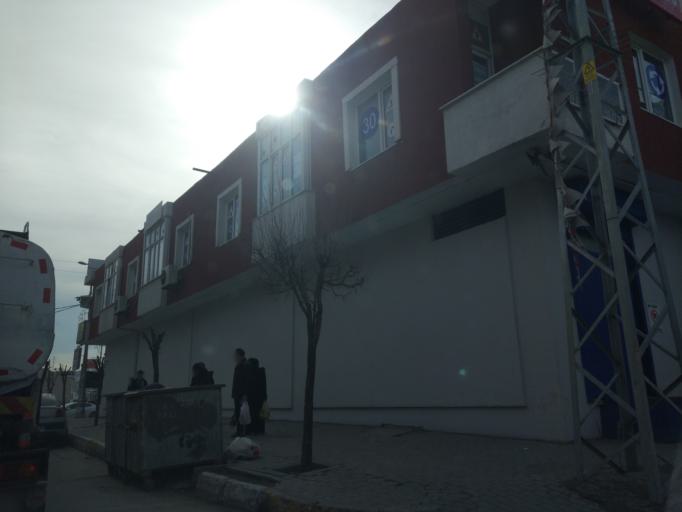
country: TR
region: Istanbul
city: Esenyurt
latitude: 41.0318
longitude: 28.7024
